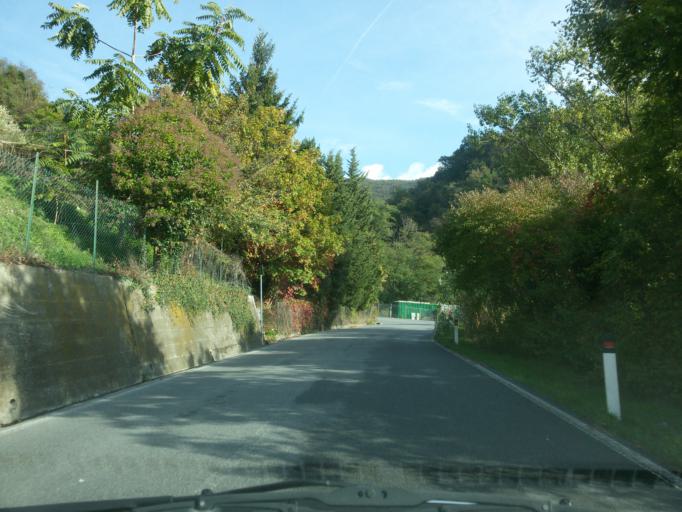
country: IT
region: Liguria
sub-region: Provincia di Genova
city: Piccarello
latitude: 44.4827
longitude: 8.9724
